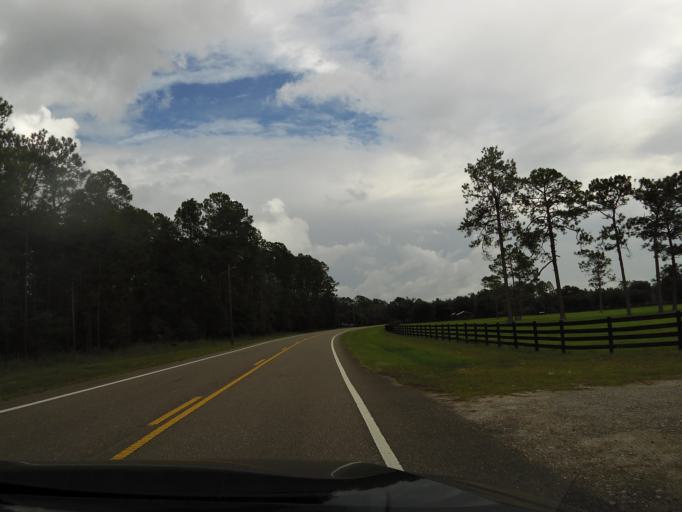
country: US
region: Florida
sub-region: Duval County
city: Baldwin
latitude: 30.3652
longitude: -81.9221
